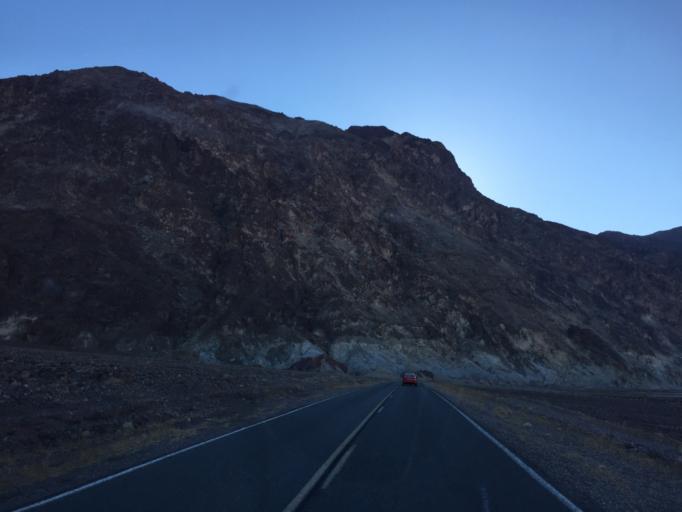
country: US
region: Nevada
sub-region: Nye County
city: Beatty
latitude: 36.1797
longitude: -116.7677
